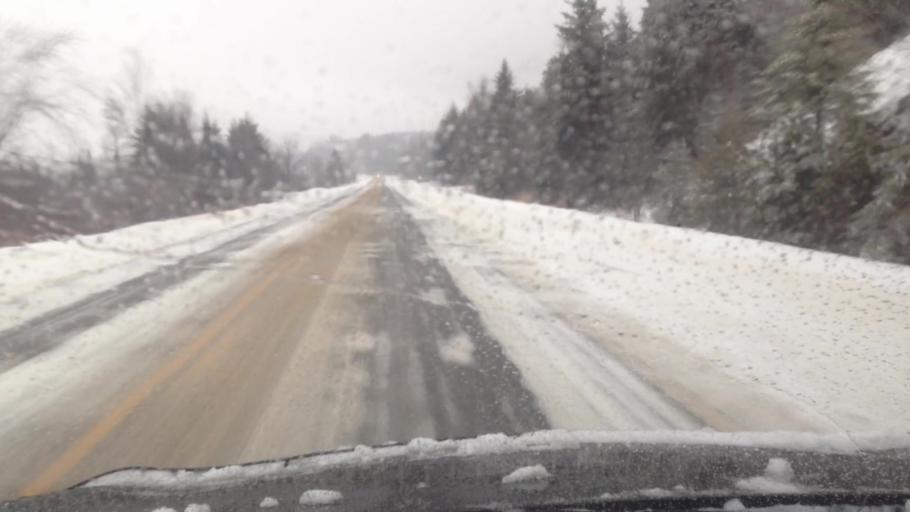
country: CA
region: Quebec
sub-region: Laurentides
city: Mont-Tremblant
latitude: 46.0748
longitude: -74.6199
